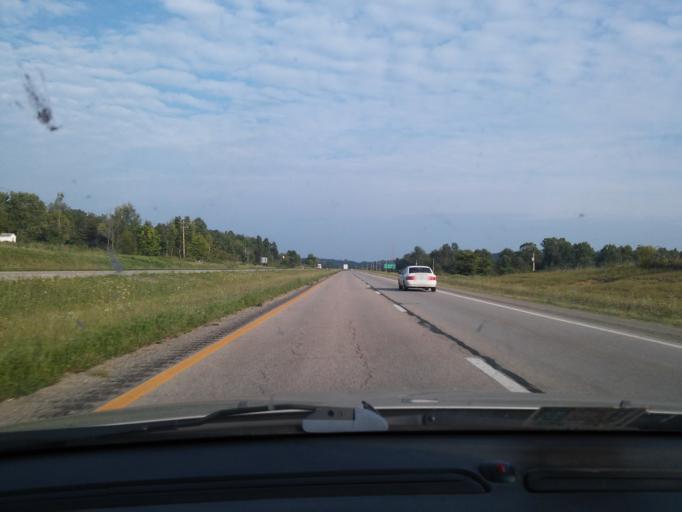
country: US
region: Ohio
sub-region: Jackson County
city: Oak Hill
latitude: 38.8920
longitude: -82.4342
